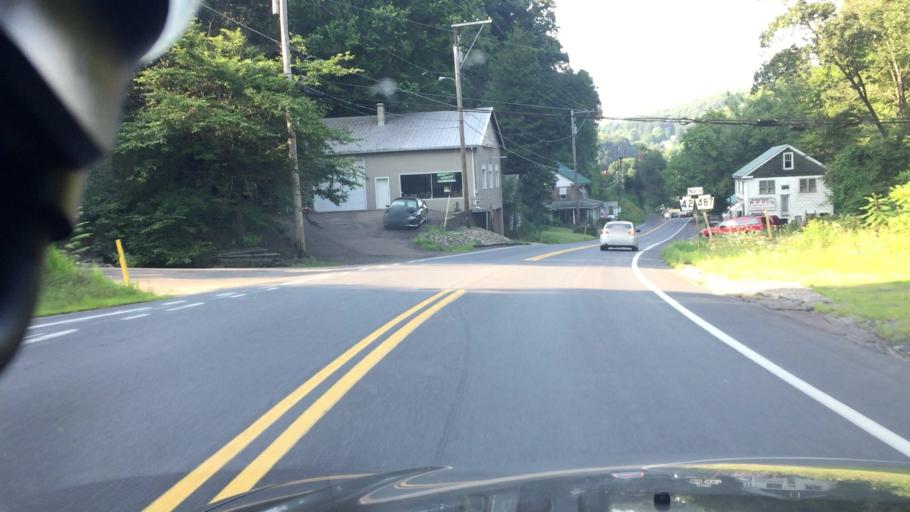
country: US
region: Pennsylvania
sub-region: Columbia County
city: Catawissa
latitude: 40.9428
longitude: -76.4572
